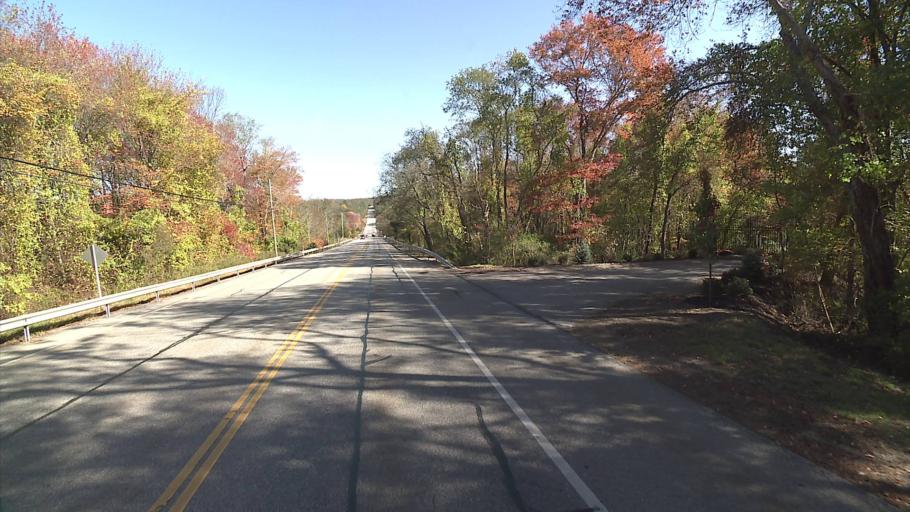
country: US
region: Connecticut
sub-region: Windham County
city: Windham
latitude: 41.7694
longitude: -72.0480
